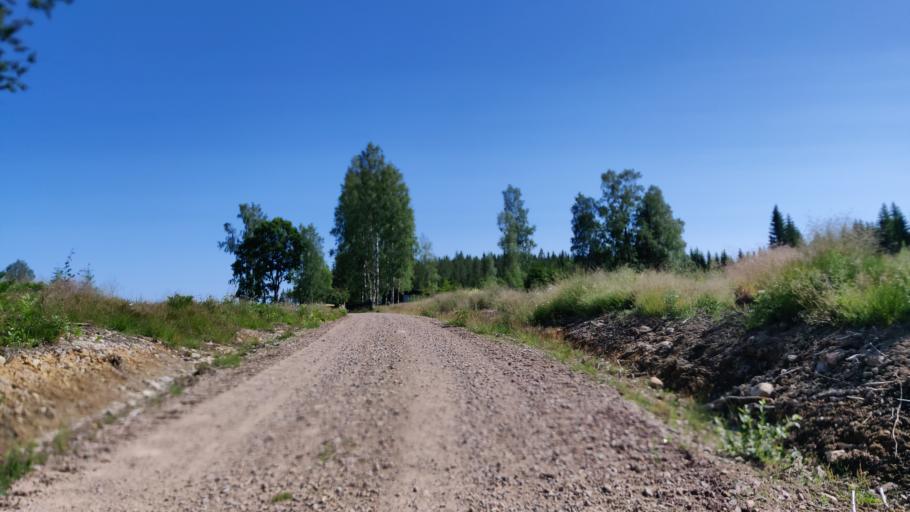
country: SE
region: Vaermland
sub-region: Hagfors Kommun
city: Hagfors
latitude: 59.9710
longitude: 13.6073
